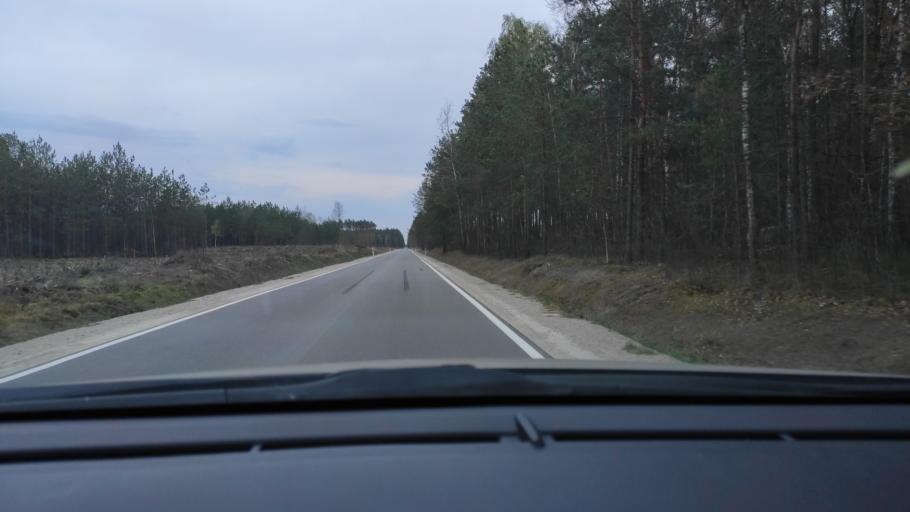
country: PL
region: Masovian Voivodeship
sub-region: Powiat zwolenski
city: Zwolen
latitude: 51.4000
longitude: 21.5384
